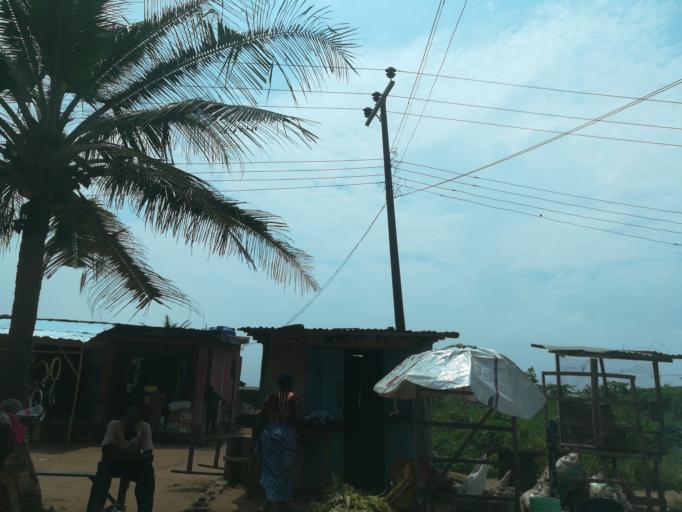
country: NG
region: Lagos
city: Ikorodu
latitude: 6.5894
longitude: 3.6244
